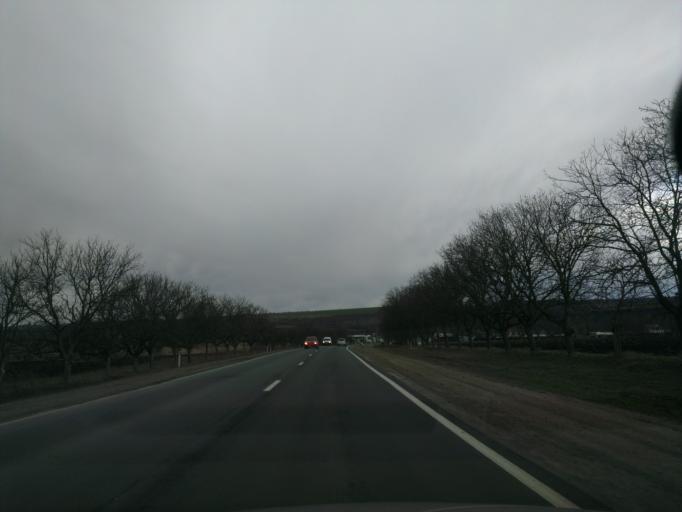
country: MD
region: Chisinau
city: Stauceni
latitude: 47.0897
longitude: 28.8369
